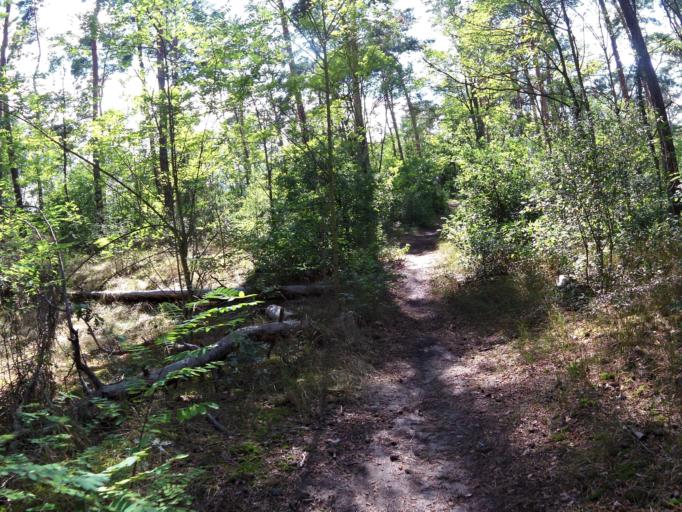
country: DE
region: Brandenburg
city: Storkow
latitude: 52.2619
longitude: 13.9471
